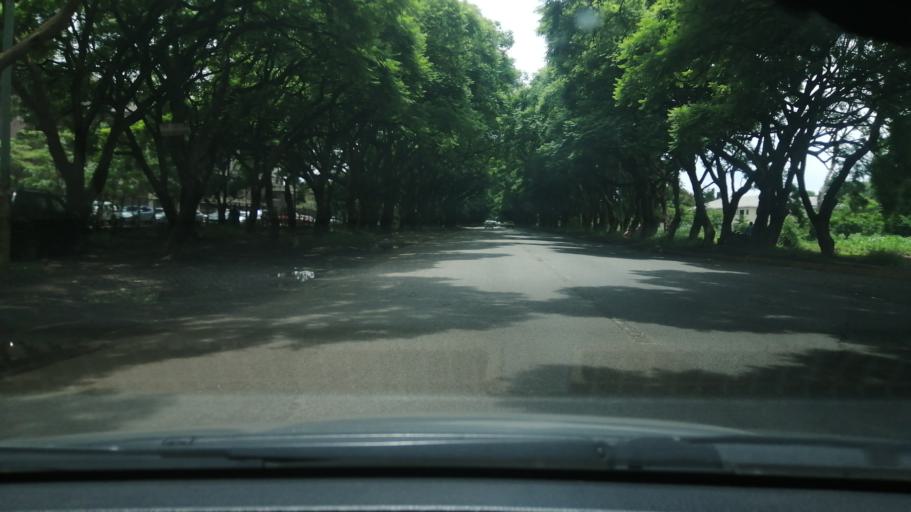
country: ZW
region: Harare
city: Harare
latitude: -17.8095
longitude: 31.0406
